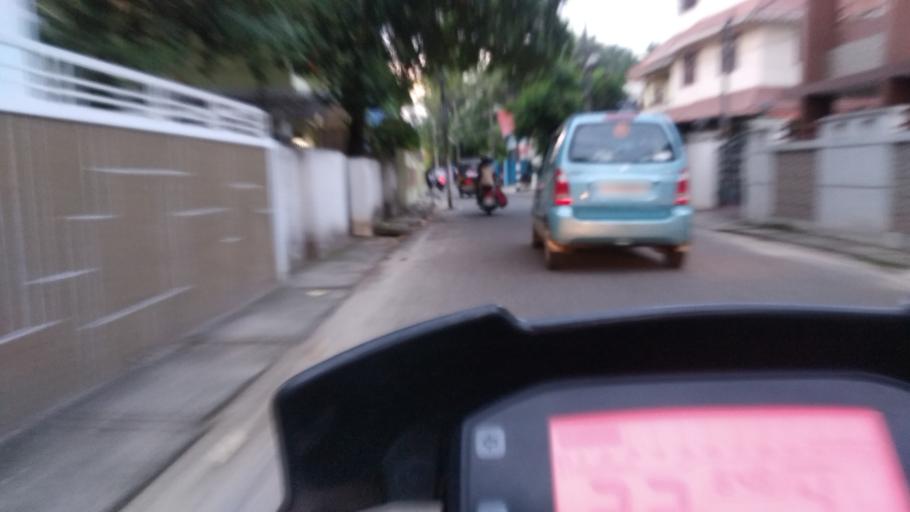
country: IN
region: Kerala
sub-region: Ernakulam
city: Elur
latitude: 10.0085
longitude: 76.2763
